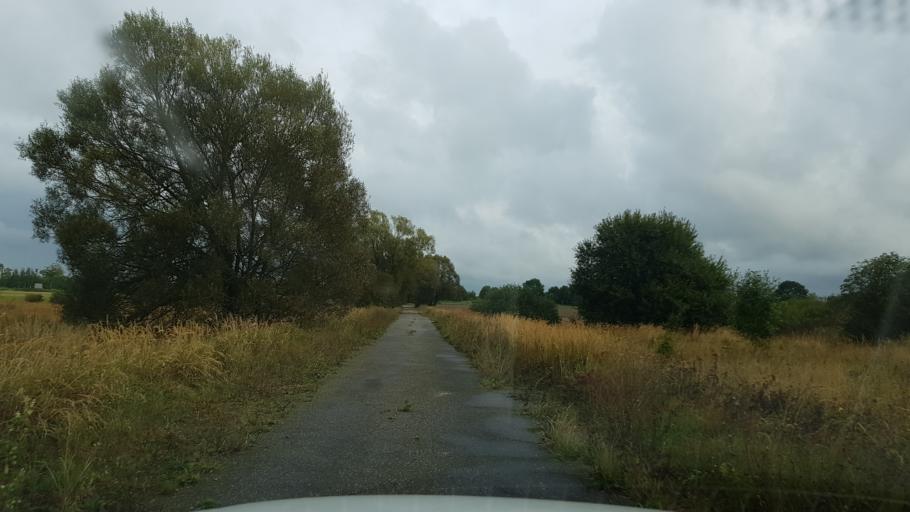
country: PL
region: West Pomeranian Voivodeship
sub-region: Powiat gryficki
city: Trzebiatow
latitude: 54.0768
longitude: 15.2146
